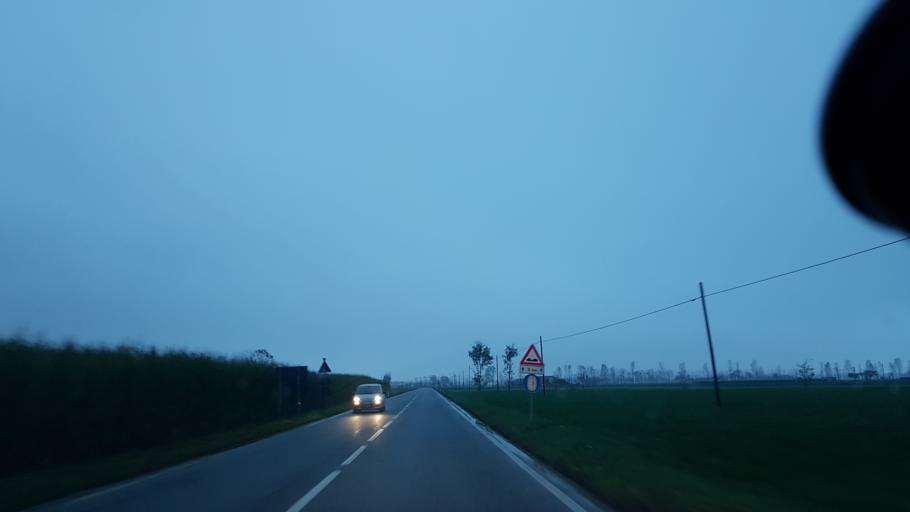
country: IT
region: Piedmont
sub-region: Provincia di Cuneo
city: Genola
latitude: 44.5570
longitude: 7.6555
